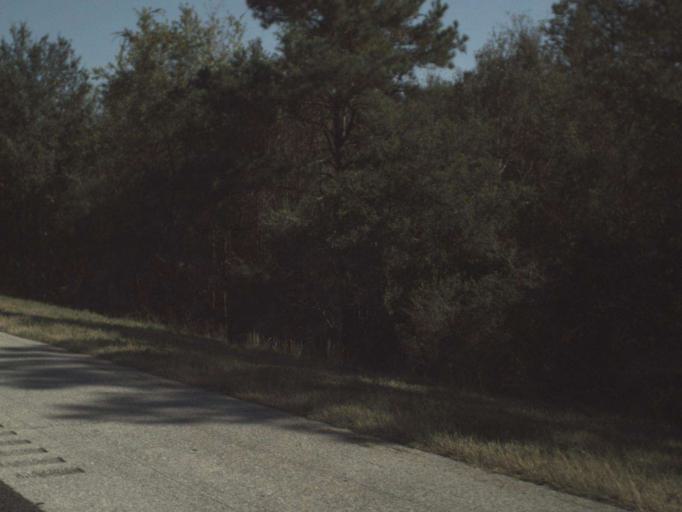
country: US
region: Florida
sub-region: Holmes County
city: Bonifay
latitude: 30.7605
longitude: -85.7894
